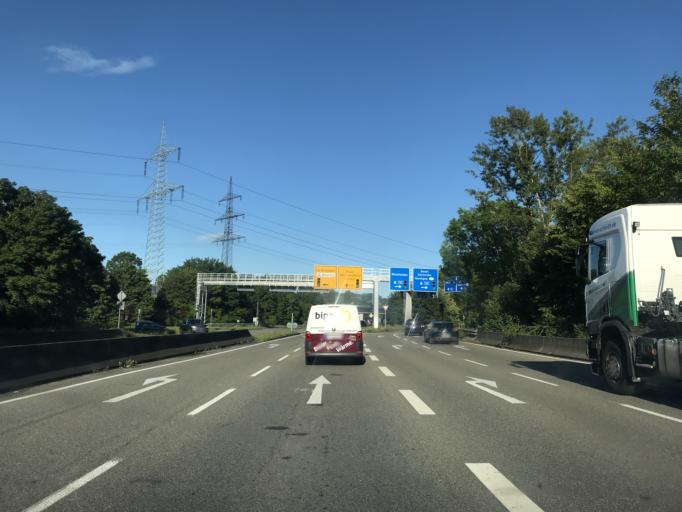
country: DE
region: Baden-Wuerttemberg
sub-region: Freiburg Region
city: Loerrach
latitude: 47.6327
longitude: 7.6768
